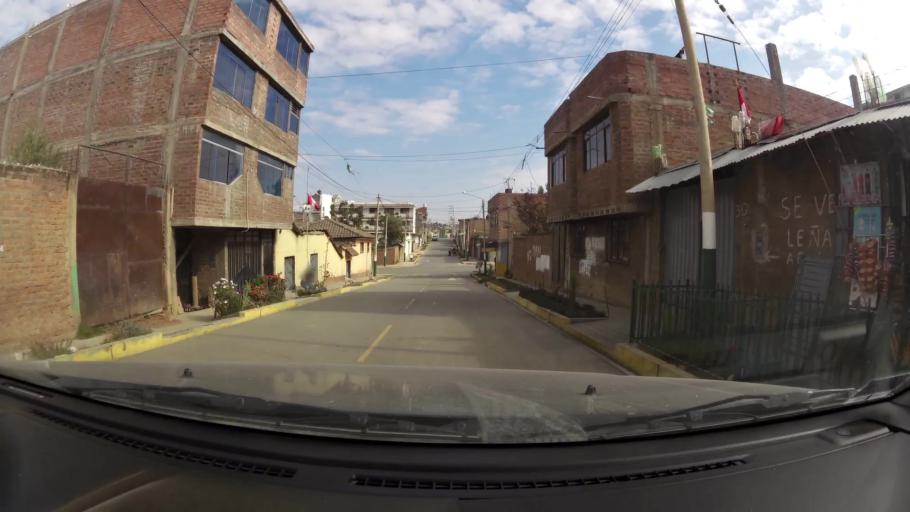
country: PE
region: Junin
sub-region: Provincia de Huancayo
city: Huancayo
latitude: -12.0546
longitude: -75.1978
